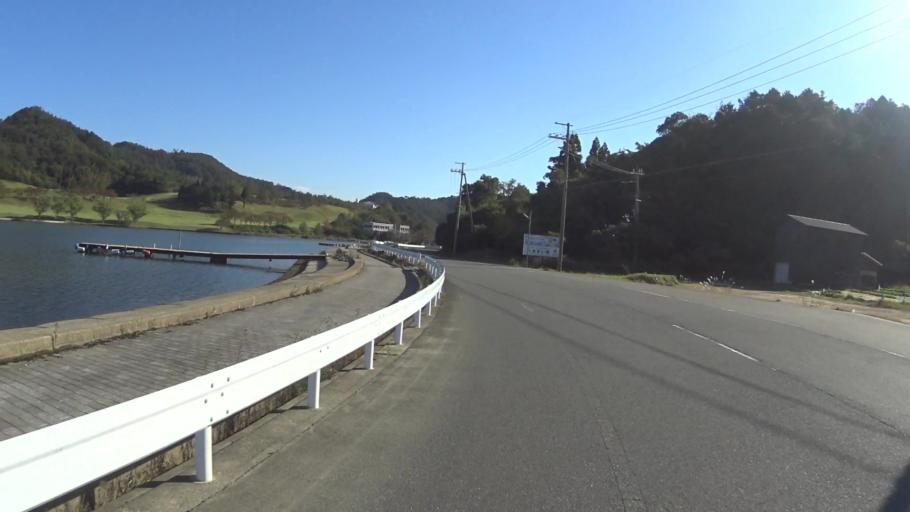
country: JP
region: Hyogo
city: Toyooka
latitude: 35.6310
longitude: 134.8877
